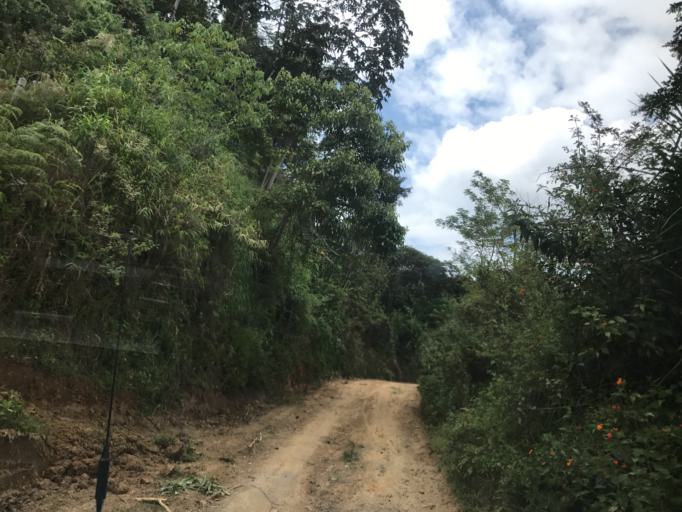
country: CO
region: Valle del Cauca
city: Obando
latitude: 4.5526
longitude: -75.9185
